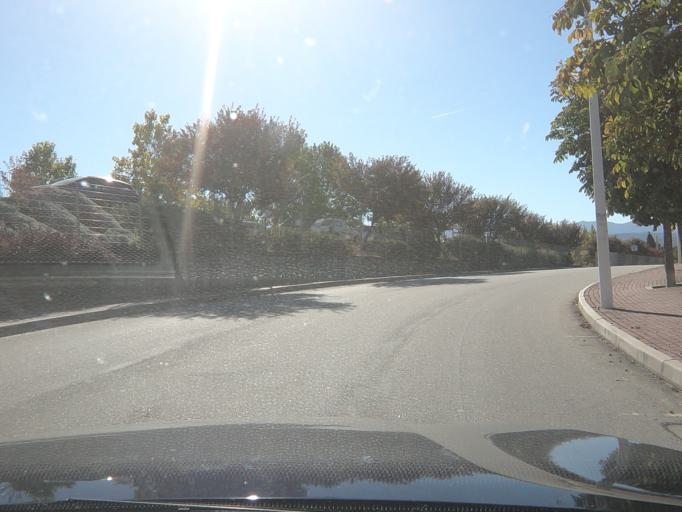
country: PT
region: Vila Real
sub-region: Vila Real
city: Vila Real
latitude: 41.2846
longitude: -7.7352
